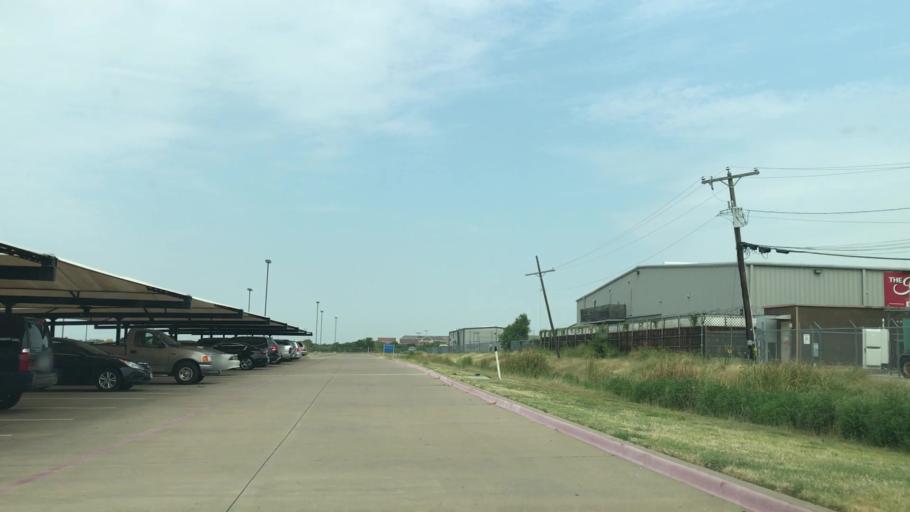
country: US
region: Texas
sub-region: Tarrant County
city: Keller
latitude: 32.9091
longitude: -97.2574
